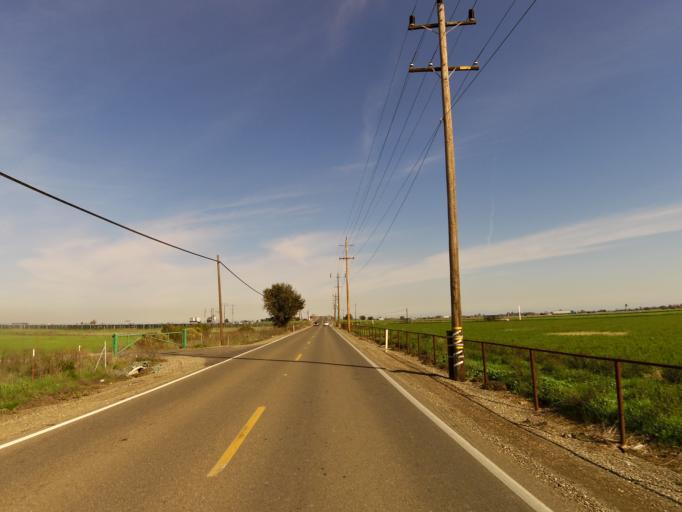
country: US
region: California
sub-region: Sacramento County
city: Walnut Grove
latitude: 38.2808
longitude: -121.4635
